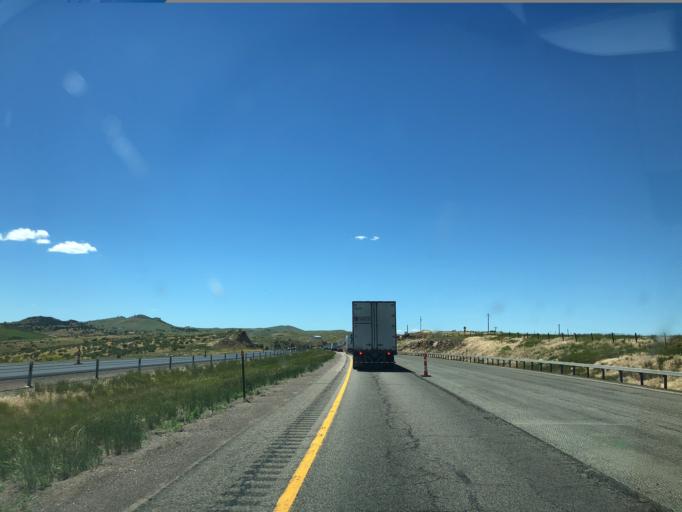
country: US
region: Wyoming
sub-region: Laramie County
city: Cheyenne
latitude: 41.0999
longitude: -105.1541
